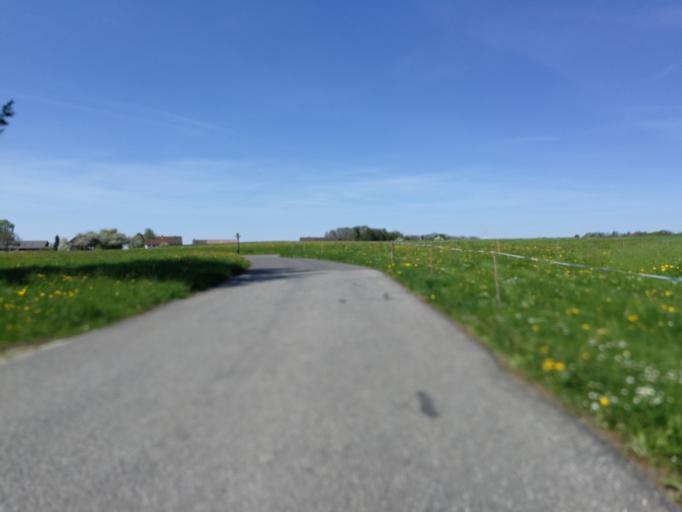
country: CH
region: Zurich
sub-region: Bezirk Hinwil
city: Bubikon
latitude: 47.2721
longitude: 8.8098
